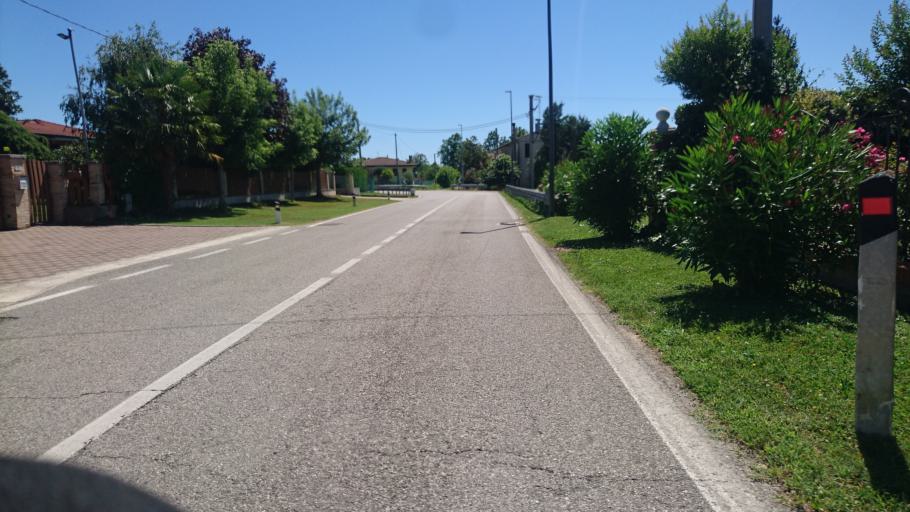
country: IT
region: Veneto
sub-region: Provincia di Padova
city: Campagnola
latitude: 45.2842
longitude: 12.0043
